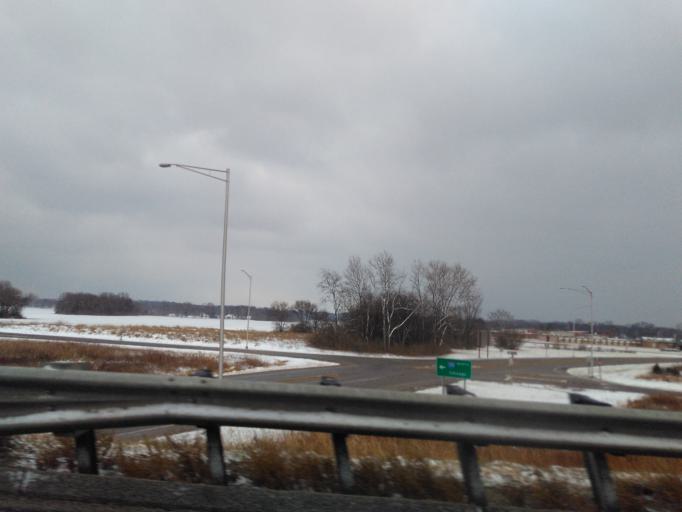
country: US
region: Illinois
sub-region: Saint Clair County
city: Centreville
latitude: 38.5654
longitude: -90.1305
